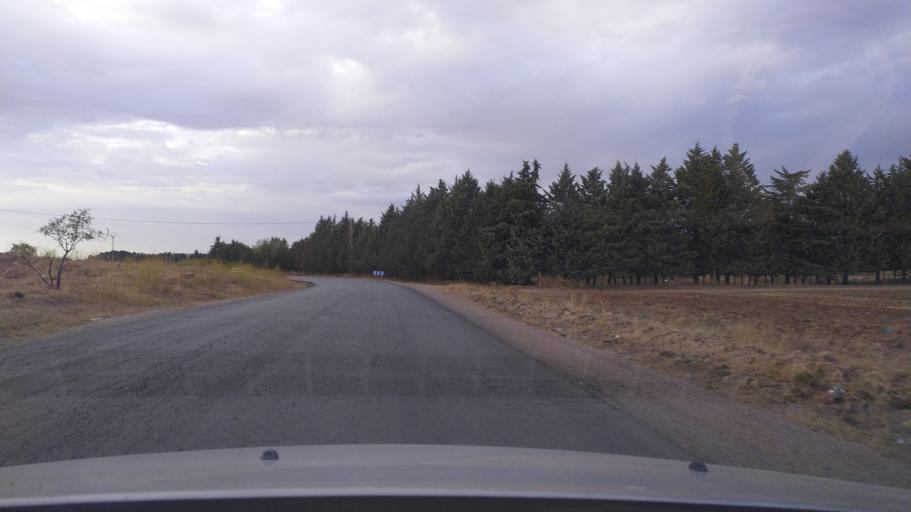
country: DZ
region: Tiaret
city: Frenda
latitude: 35.0297
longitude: 1.0938
